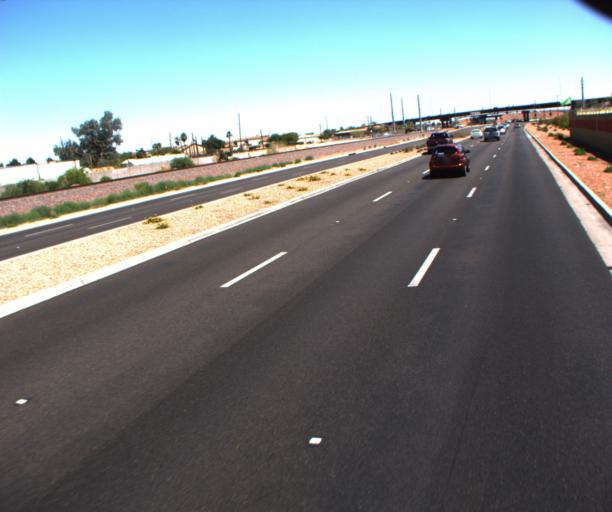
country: US
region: Arizona
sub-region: Maricopa County
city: Peoria
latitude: 33.5693
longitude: -112.2234
